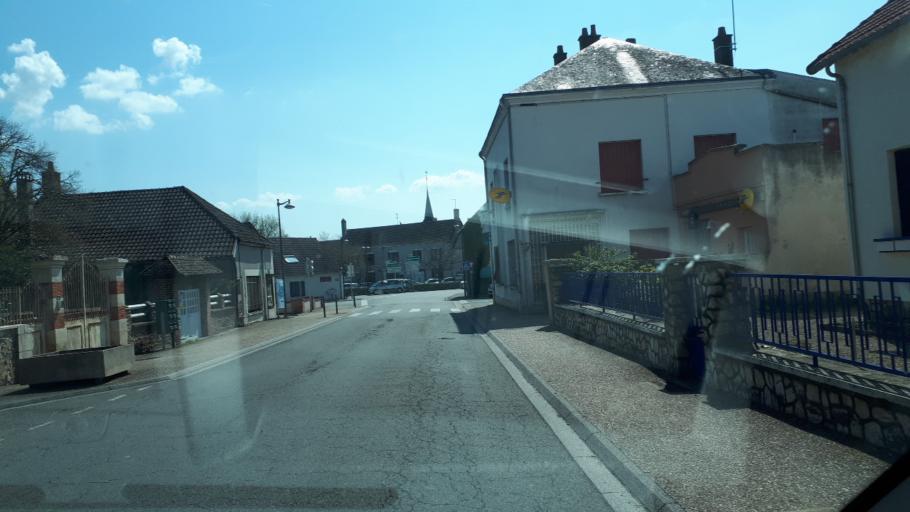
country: FR
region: Centre
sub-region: Departement du Cher
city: Neuvy-sur-Barangeon
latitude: 47.3155
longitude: 2.2537
